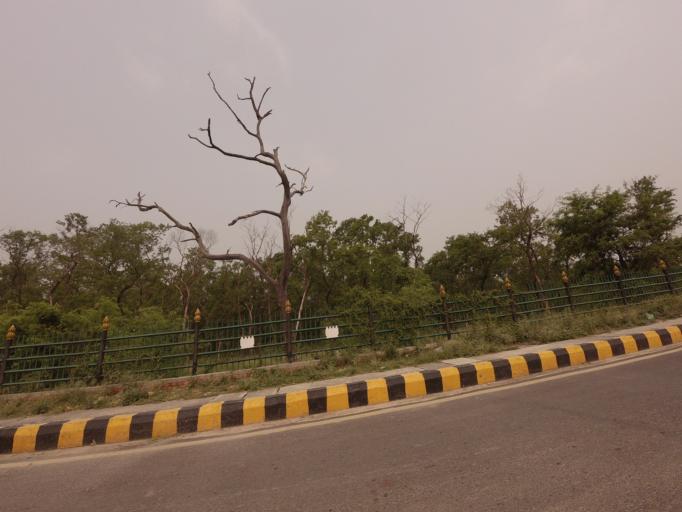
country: IN
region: Uttar Pradesh
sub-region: Maharajganj
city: Nautanwa
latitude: 27.4899
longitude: 83.2843
